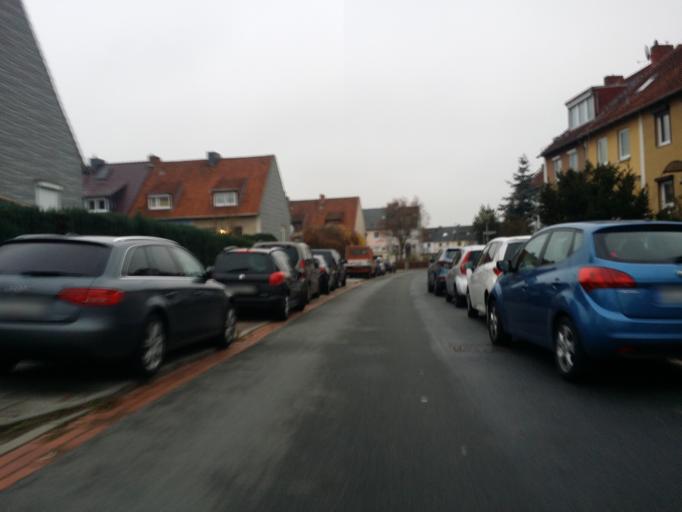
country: DE
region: Bremen
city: Bremen
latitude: 53.0290
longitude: 8.8198
